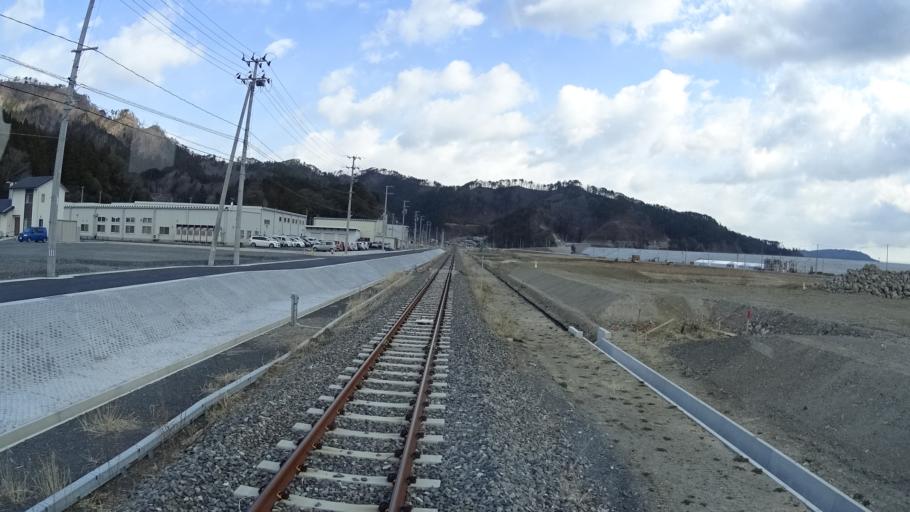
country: JP
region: Iwate
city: Otsuchi
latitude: 39.3337
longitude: 141.8913
